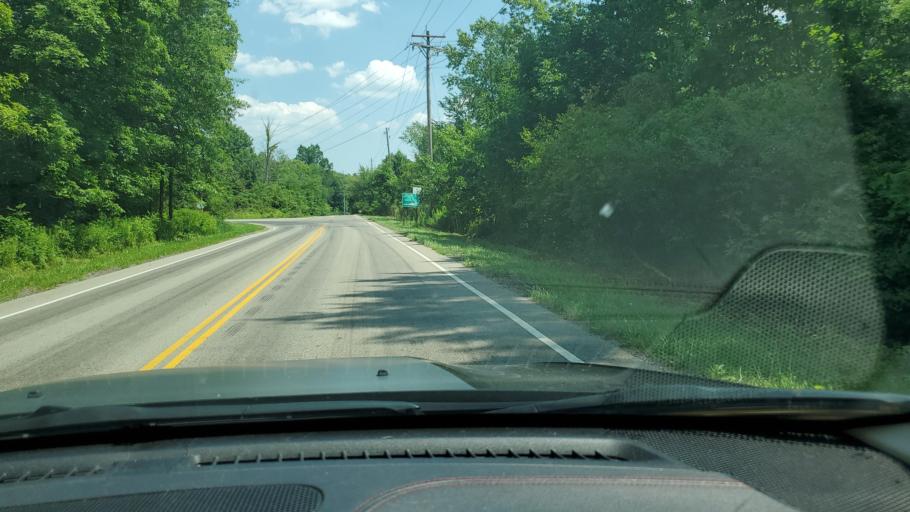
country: US
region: Ohio
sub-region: Trumbull County
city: Bolindale
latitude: 41.2035
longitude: -80.7980
